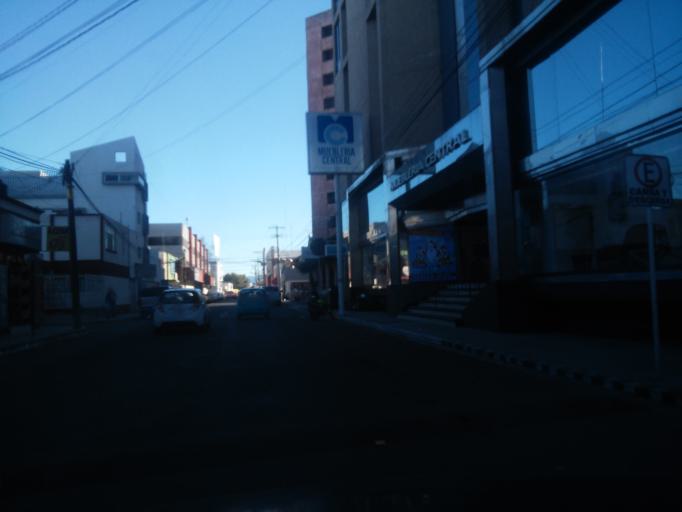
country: MX
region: Durango
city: Victoria de Durango
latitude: 24.0304
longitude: -104.6477
